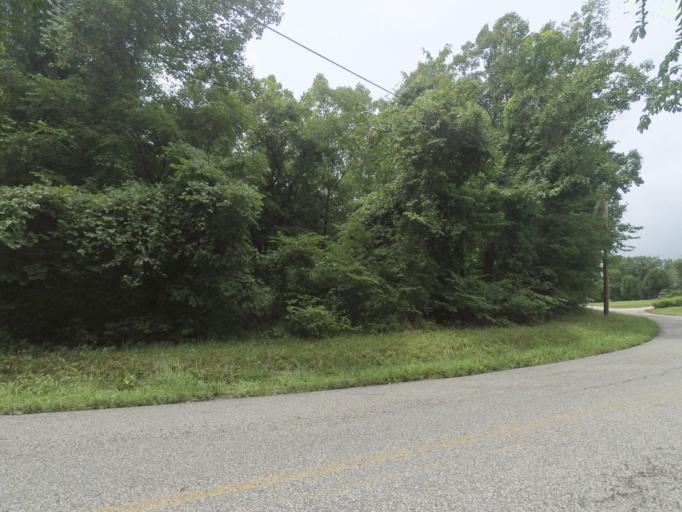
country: US
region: West Virginia
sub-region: Cabell County
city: Huntington
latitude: 38.4326
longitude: -82.4690
